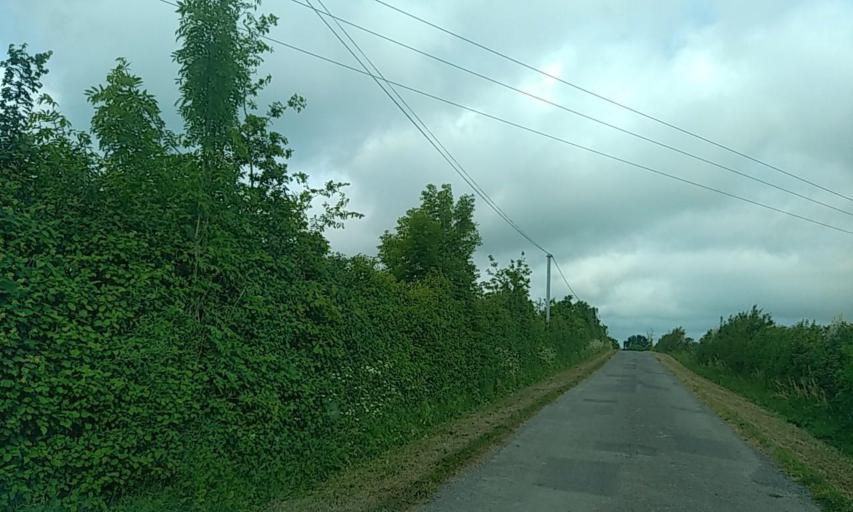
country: FR
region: Poitou-Charentes
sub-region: Departement des Deux-Sevres
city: Boisme
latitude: 46.7640
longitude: -0.4169
